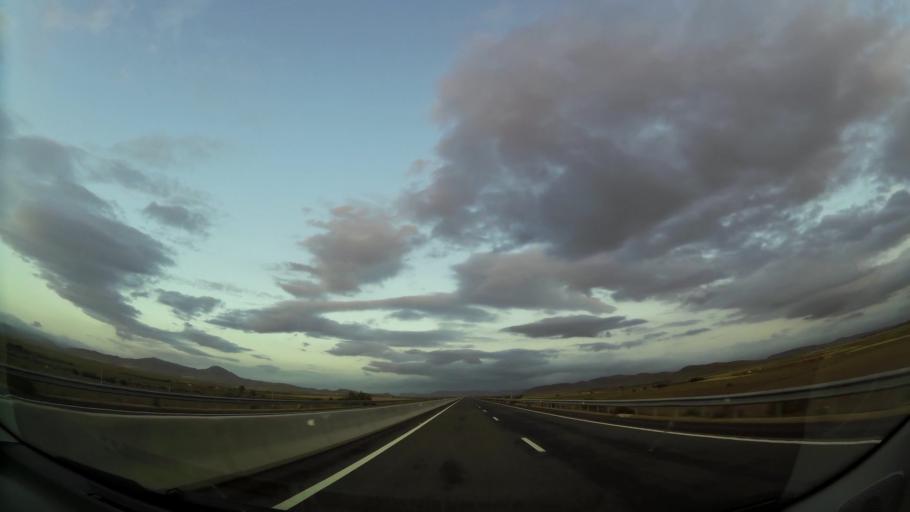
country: MA
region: Oriental
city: El Aioun
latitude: 34.6026
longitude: -2.7424
